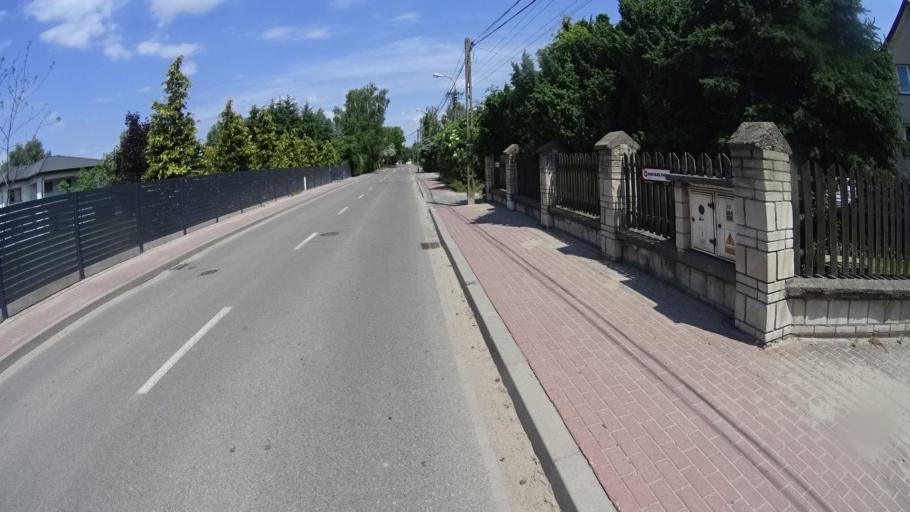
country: PL
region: Masovian Voivodeship
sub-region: Powiat warszawski zachodni
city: Stare Babice
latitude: 52.2563
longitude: 20.8314
